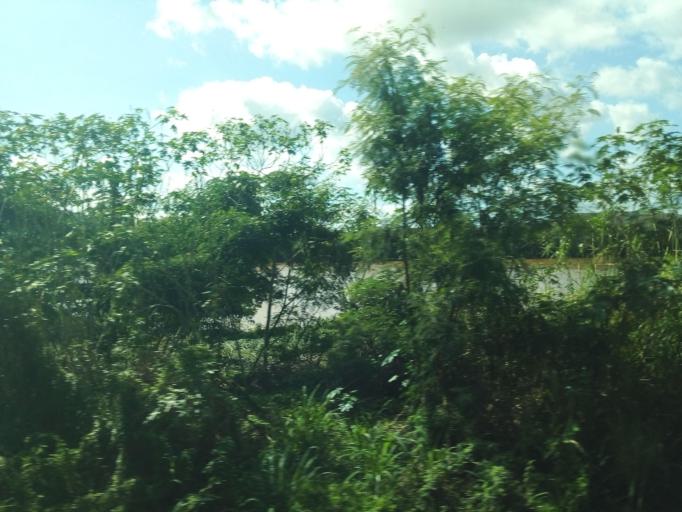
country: BR
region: Minas Gerais
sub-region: Governador Valadares
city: Governador Valadares
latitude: -18.8705
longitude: -41.7771
